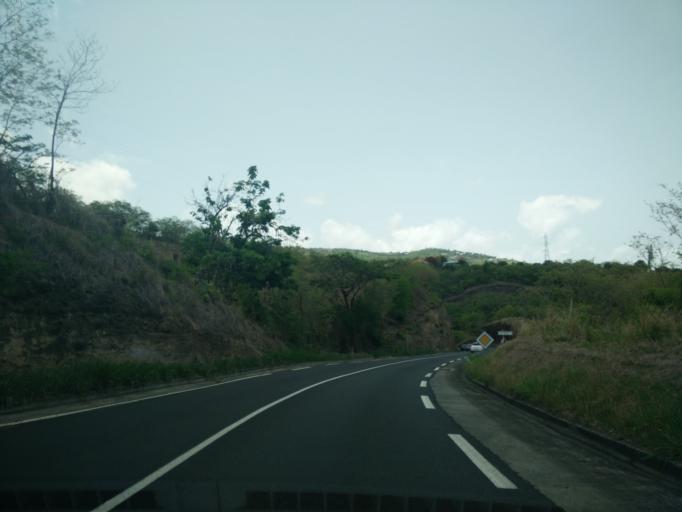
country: MQ
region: Martinique
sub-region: Martinique
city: Saint-Pierre
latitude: 14.6949
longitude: -61.1665
